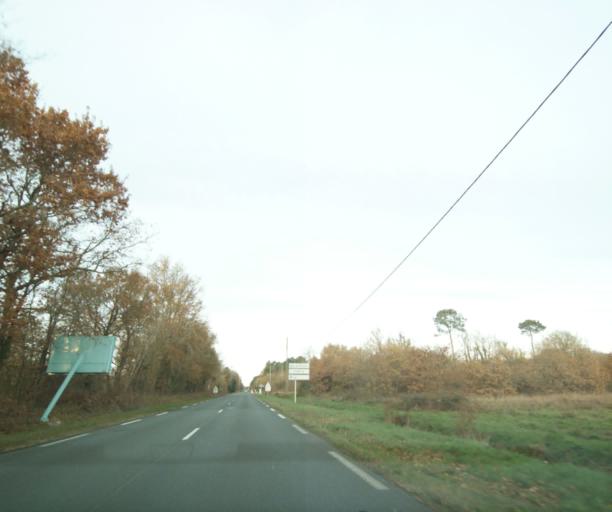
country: FR
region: Aquitaine
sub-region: Departement de la Gironde
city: Prechac
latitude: 44.2988
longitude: -0.2575
